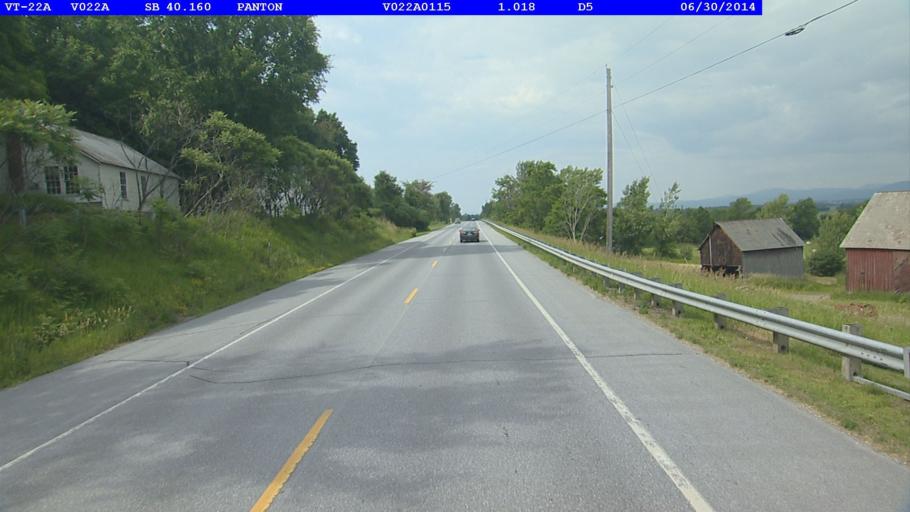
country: US
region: Vermont
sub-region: Addison County
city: Vergennes
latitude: 44.1330
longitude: -73.2856
